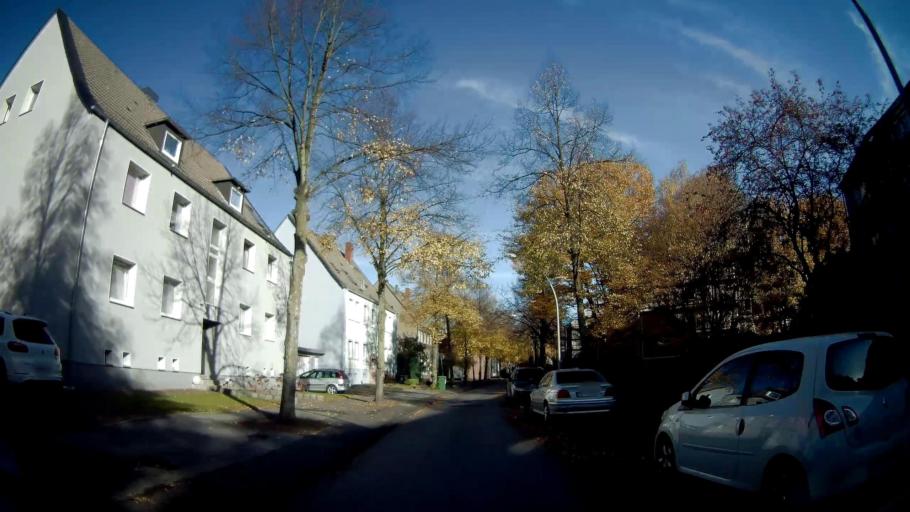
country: DE
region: North Rhine-Westphalia
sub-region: Regierungsbezirk Munster
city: Gladbeck
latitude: 51.5442
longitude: 7.0098
